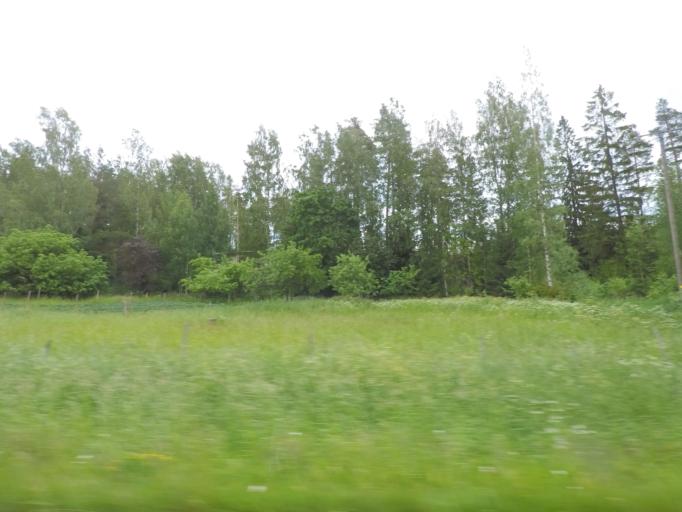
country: FI
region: Uusimaa
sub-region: Helsinki
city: Maentsaelae
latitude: 60.7491
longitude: 25.4322
